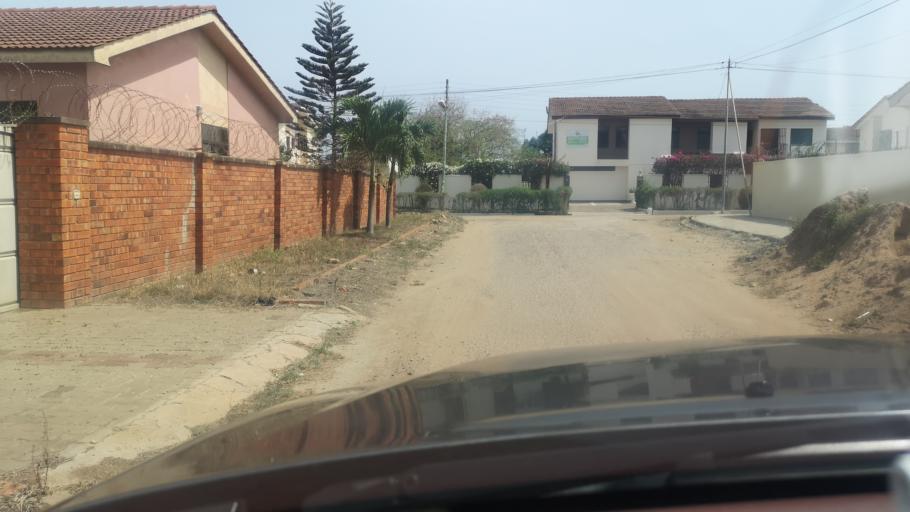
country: GH
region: Greater Accra
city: Nungua
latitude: 5.6500
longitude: -0.0748
